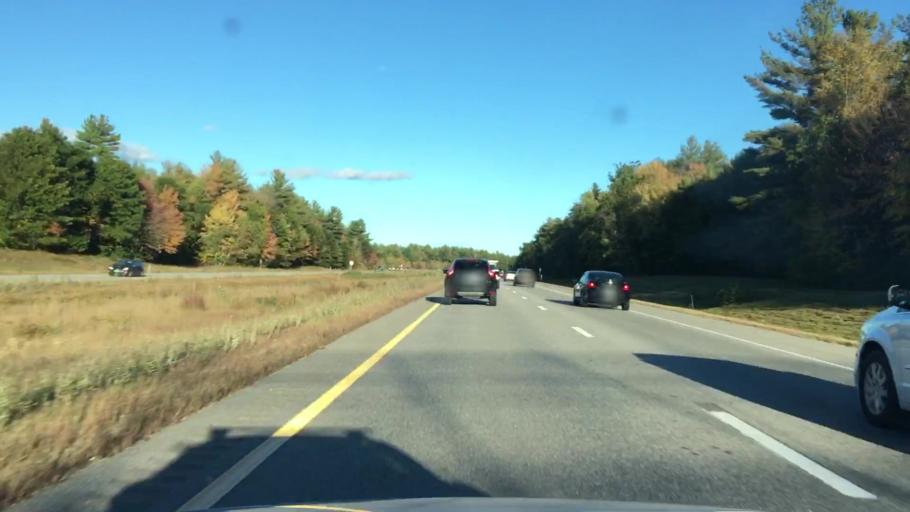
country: US
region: New Hampshire
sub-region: Rockingham County
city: Candia
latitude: 43.0418
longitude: -71.2801
